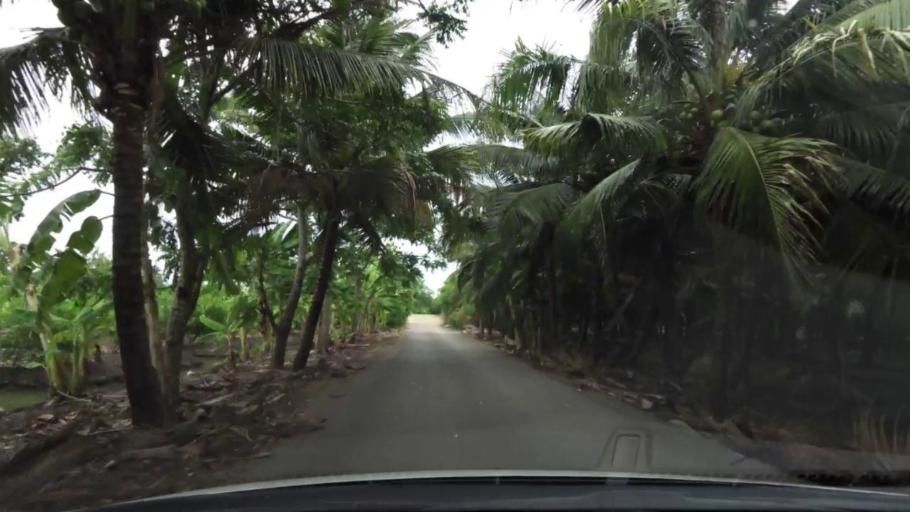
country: TH
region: Ratchaburi
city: Damnoen Saduak
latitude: 13.5509
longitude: 100.0009
